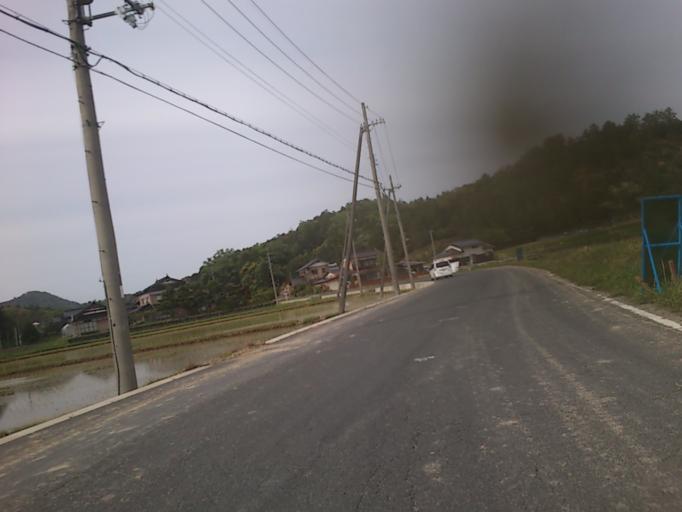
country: JP
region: Hyogo
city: Toyooka
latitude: 35.5913
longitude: 134.9443
